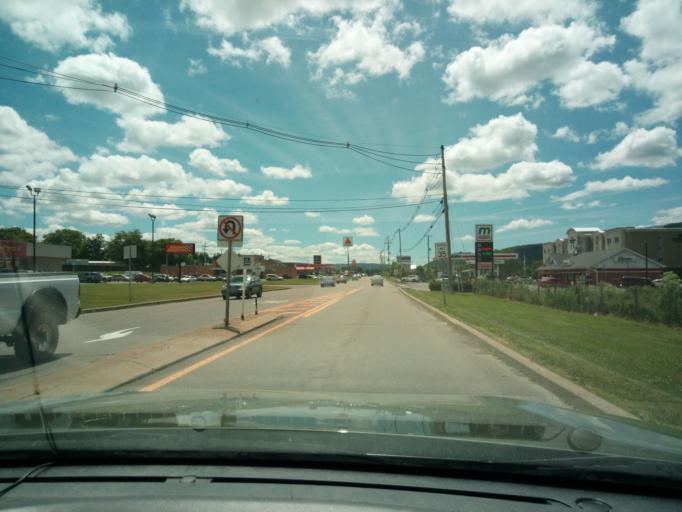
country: US
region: Pennsylvania
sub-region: Bradford County
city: South Waverly
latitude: 41.9889
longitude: -76.5470
